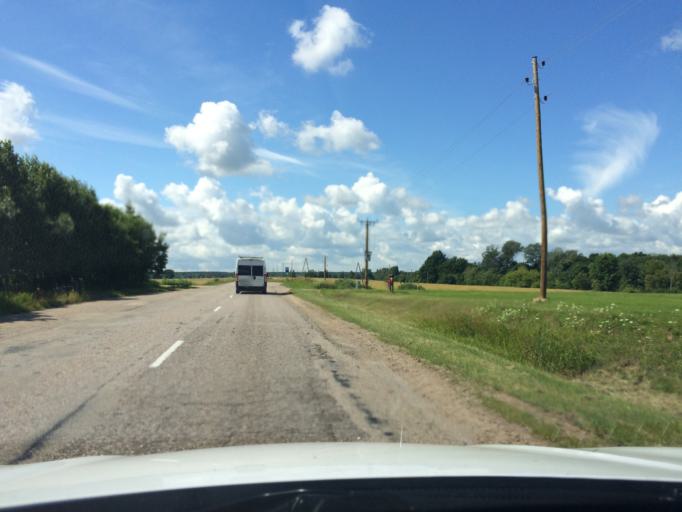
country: LV
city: Tervete
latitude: 56.5091
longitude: 23.4692
